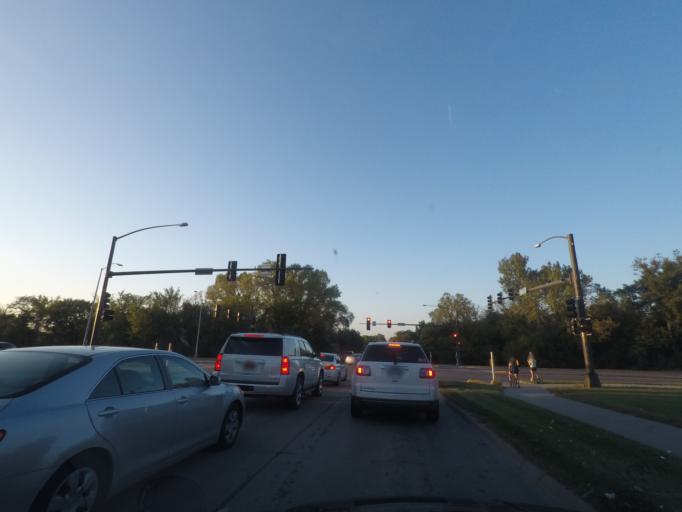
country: US
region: Iowa
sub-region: Story County
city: Ames
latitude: 42.0353
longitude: -93.6447
